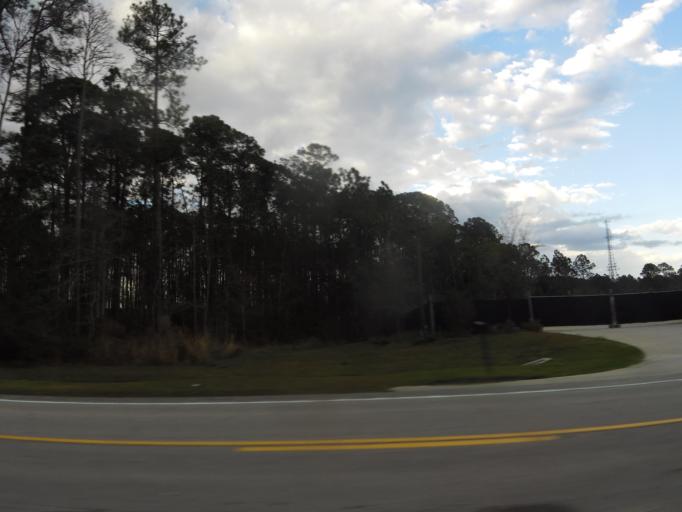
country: US
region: Florida
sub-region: Saint Johns County
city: Fruit Cove
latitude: 30.1835
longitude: -81.5726
